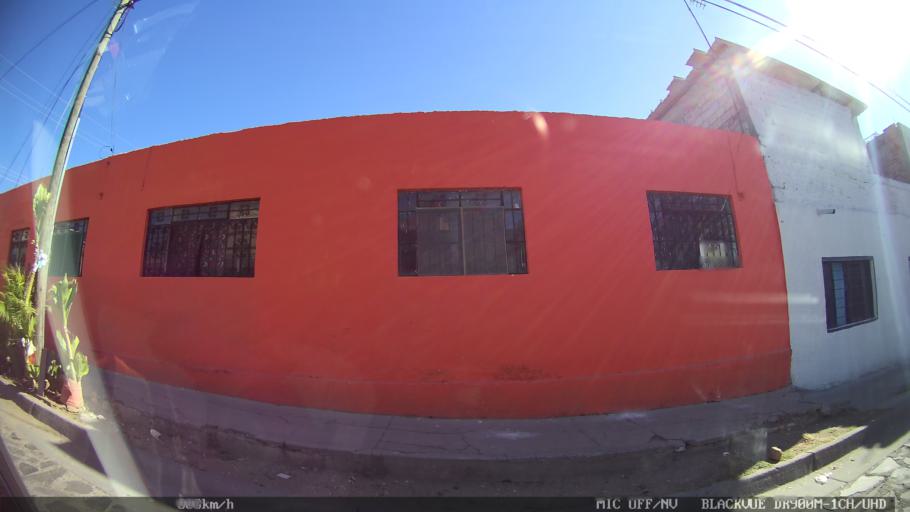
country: MX
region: Jalisco
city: Tlaquepaque
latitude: 20.6896
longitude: -103.2718
